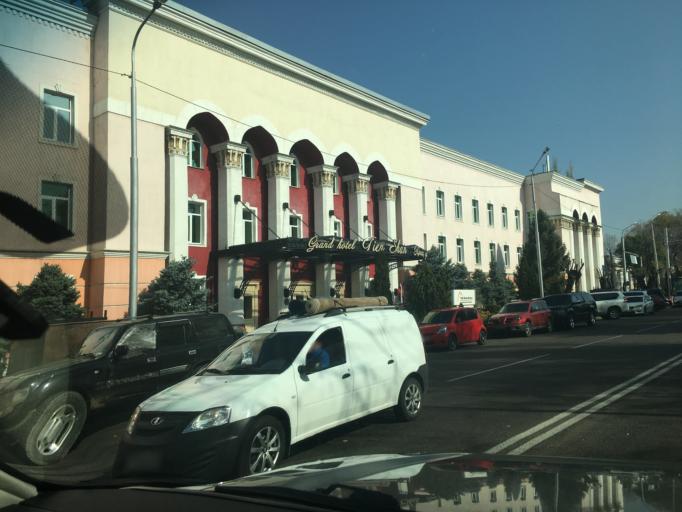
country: KZ
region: Almaty Qalasy
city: Almaty
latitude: 43.2534
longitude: 76.9493
